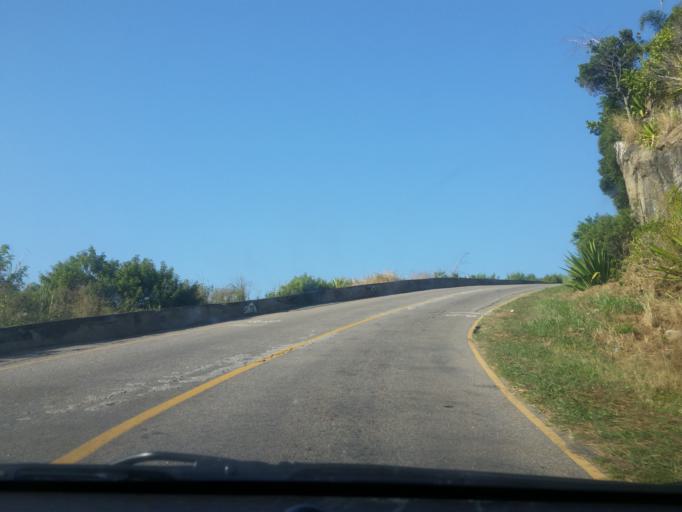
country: BR
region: Rio de Janeiro
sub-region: Nilopolis
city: Nilopolis
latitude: -23.0449
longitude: -43.5073
